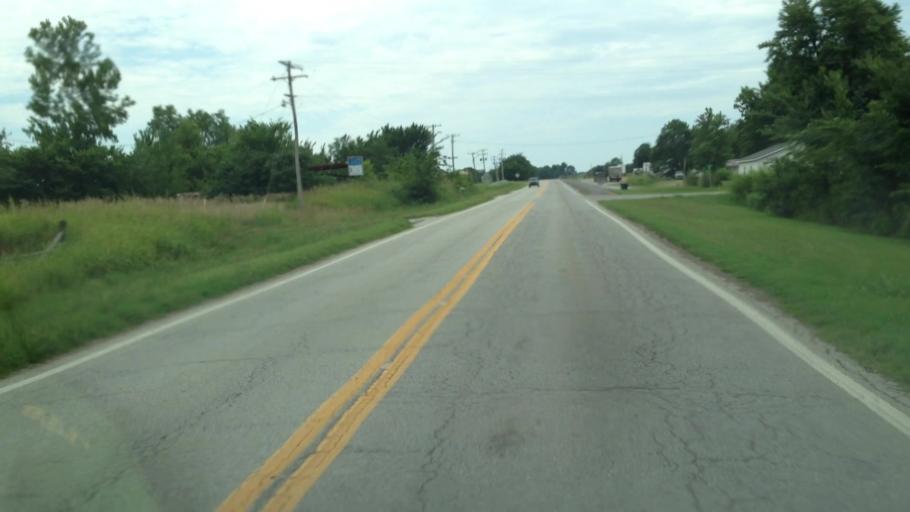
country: US
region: Kansas
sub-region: Labette County
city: Chetopa
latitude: 36.8772
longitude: -95.0989
